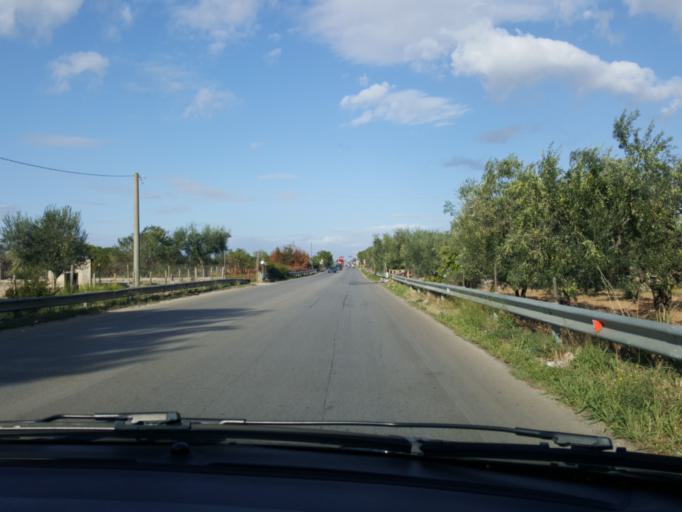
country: IT
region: Apulia
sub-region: Provincia di Bari
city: Triggiano
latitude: 41.0566
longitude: 16.9272
